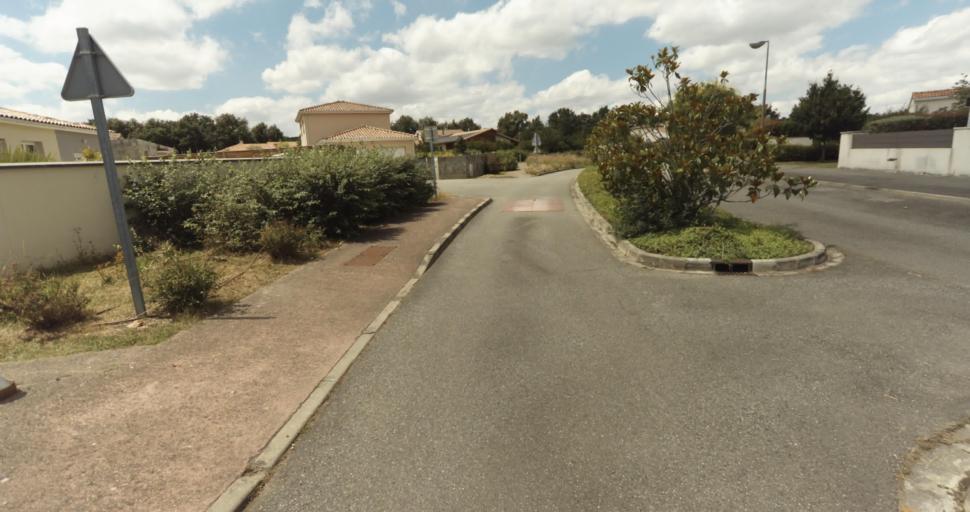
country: FR
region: Midi-Pyrenees
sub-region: Departement de la Haute-Garonne
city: Fontenilles
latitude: 43.5559
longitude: 1.1671
